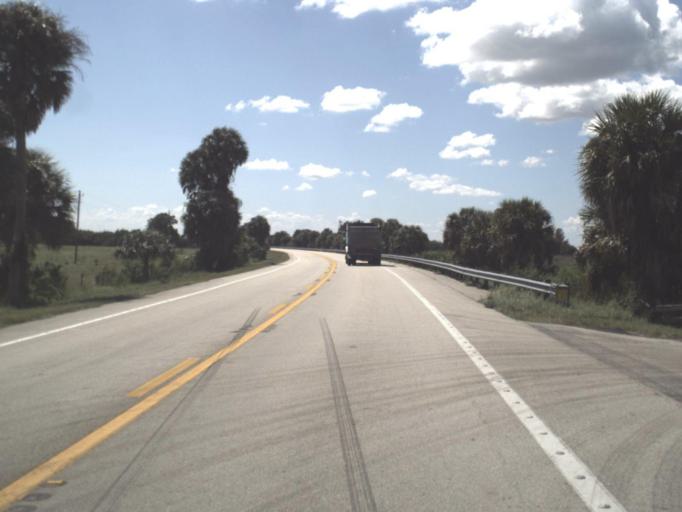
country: US
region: Florida
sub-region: Glades County
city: Buckhead Ridge
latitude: 27.1081
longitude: -80.9428
